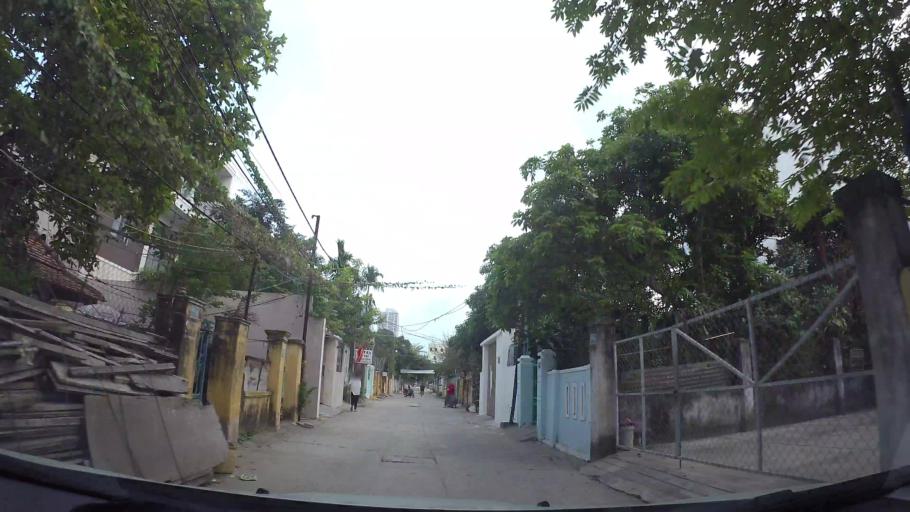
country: VN
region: Da Nang
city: Son Tra
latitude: 16.0601
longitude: 108.2443
